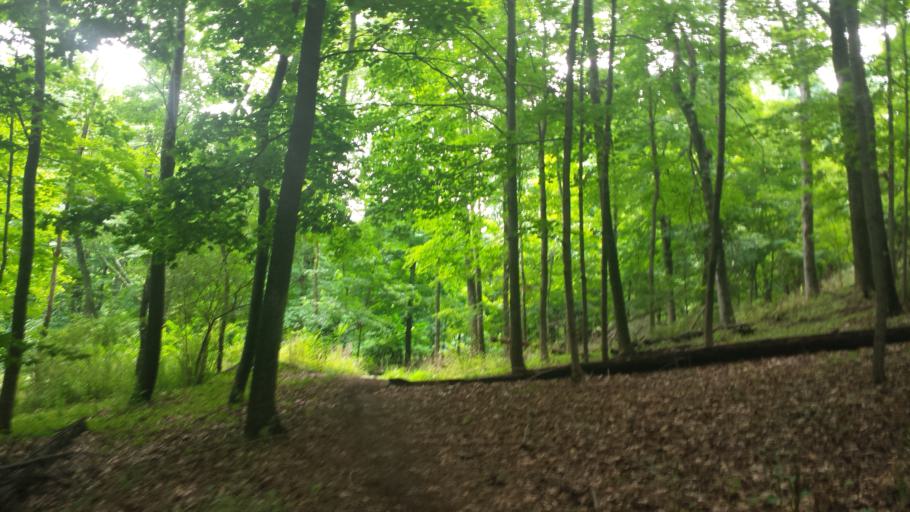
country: US
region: New York
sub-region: Westchester County
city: Thornwood
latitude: 41.1209
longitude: -73.7854
